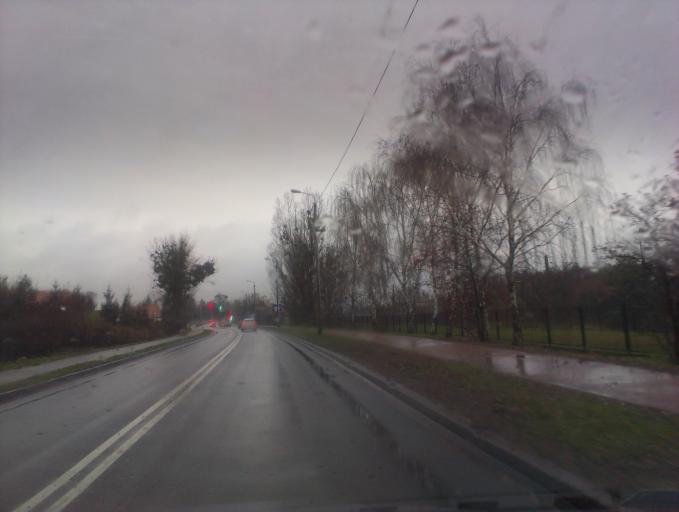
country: PL
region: Greater Poland Voivodeship
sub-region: Powiat obornicki
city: Oborniki
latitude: 52.6512
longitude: 16.8210
